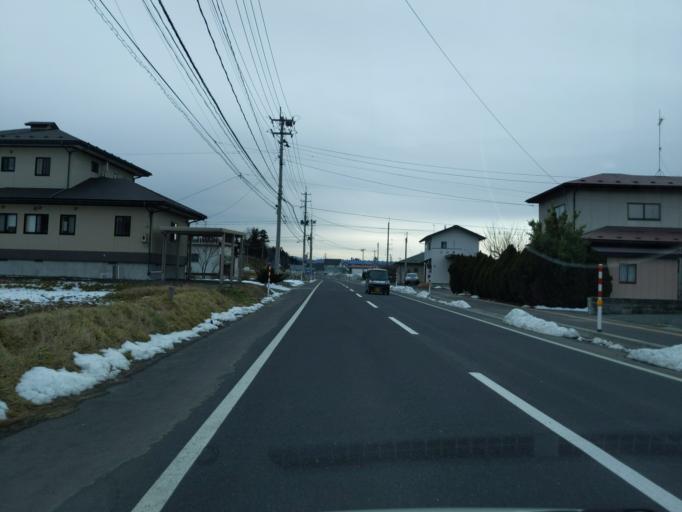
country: JP
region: Iwate
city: Mizusawa
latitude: 39.1822
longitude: 141.1896
